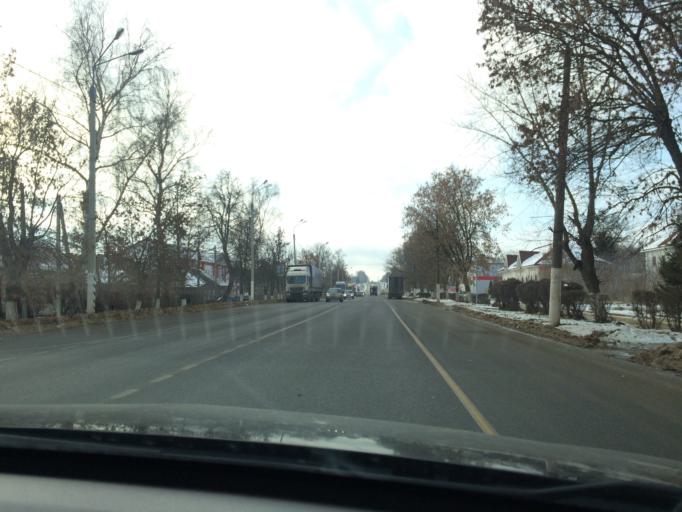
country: RU
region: Tula
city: Plavsk
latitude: 53.7039
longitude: 37.2890
